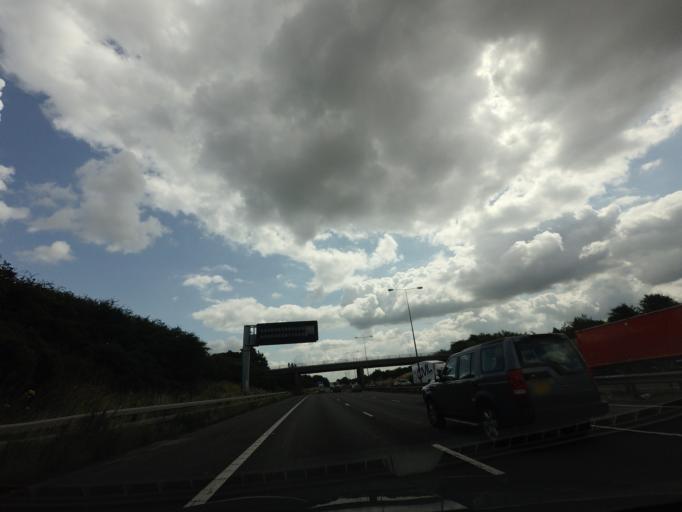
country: GB
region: England
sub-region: Borough of Wigan
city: Ashton in Makerfield
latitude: 53.5077
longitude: -2.6672
